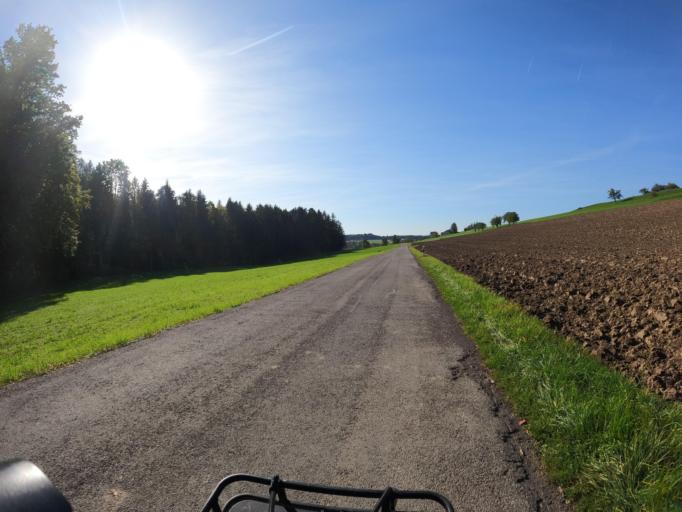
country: CH
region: Zug
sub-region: Zug
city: Baar
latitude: 47.2181
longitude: 8.5474
